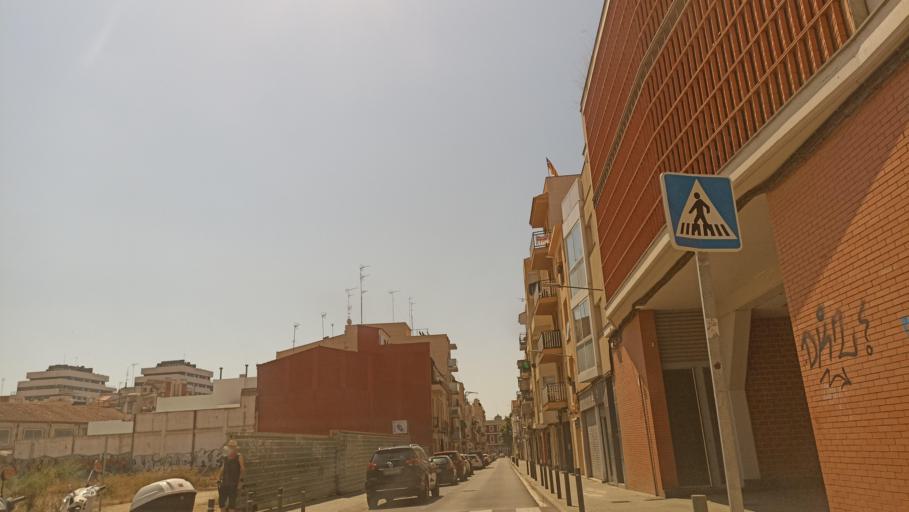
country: ES
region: Catalonia
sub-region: Provincia de Barcelona
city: Mataro
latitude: 41.5353
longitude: 2.4430
